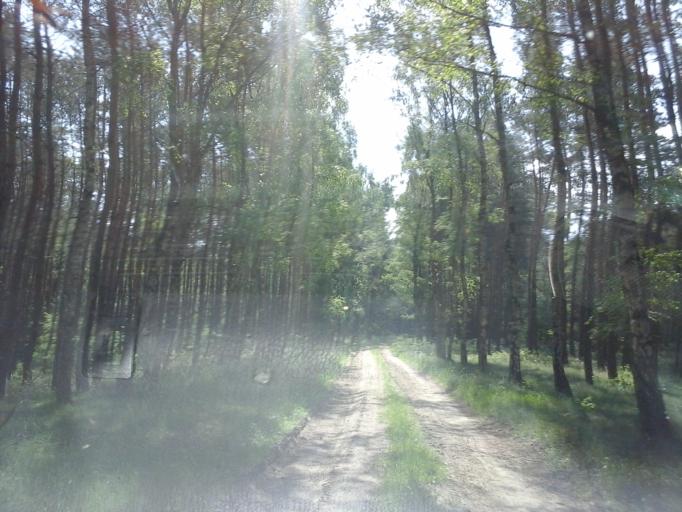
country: PL
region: West Pomeranian Voivodeship
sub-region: Powiat choszczenski
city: Recz
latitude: 53.2708
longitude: 15.6591
